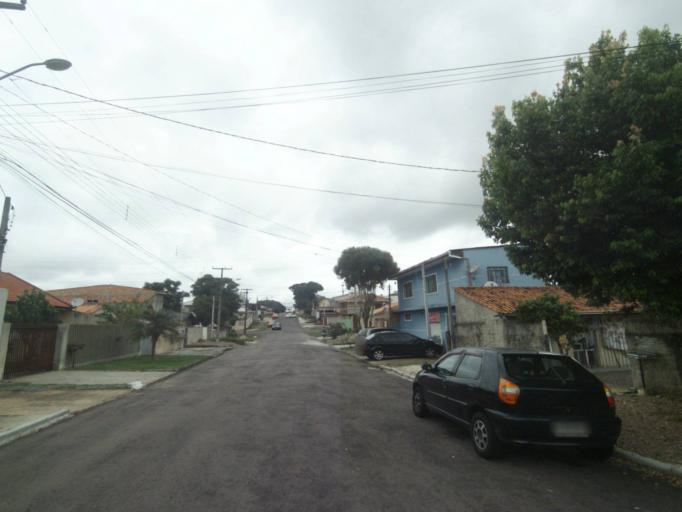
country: BR
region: Parana
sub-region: Curitiba
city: Curitiba
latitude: -25.4868
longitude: -49.3103
